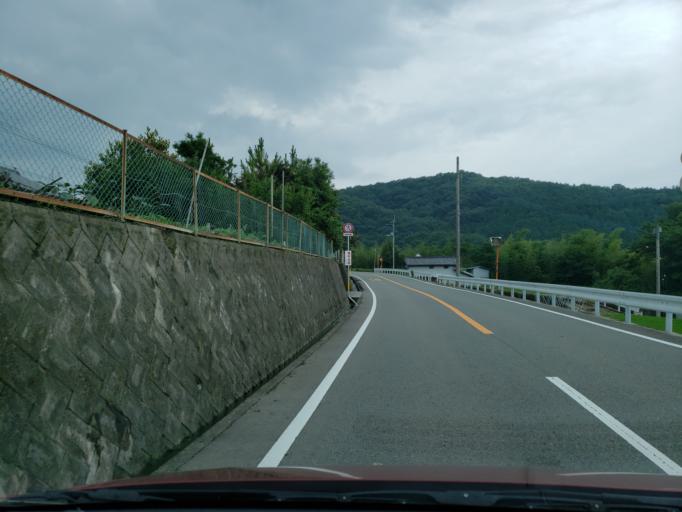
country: JP
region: Tokushima
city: Kamojimacho-jogejima
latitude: 34.1077
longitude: 134.2848
